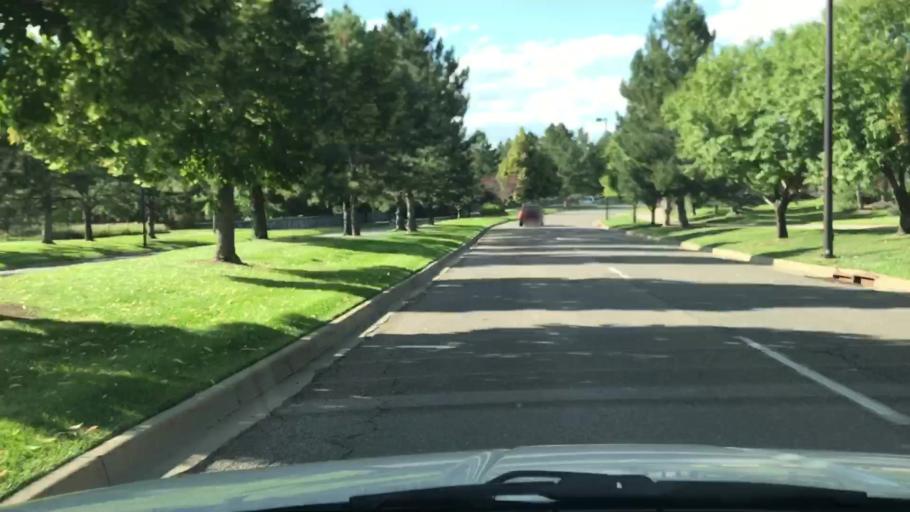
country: US
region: Colorado
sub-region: Arapahoe County
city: Greenwood Village
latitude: 39.6359
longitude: -104.9124
